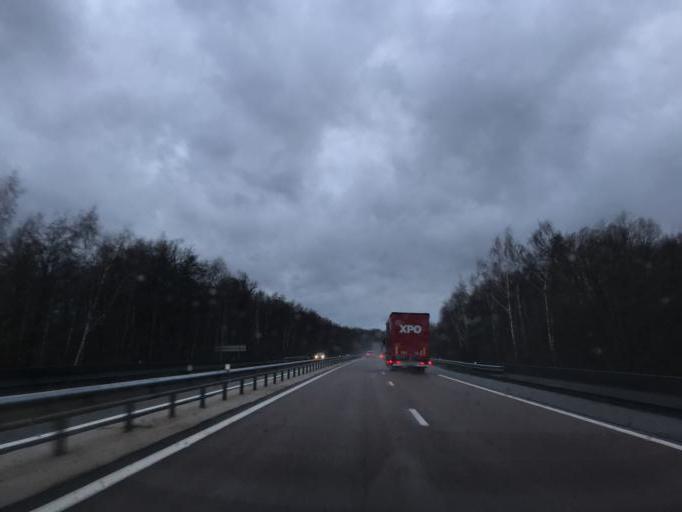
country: FR
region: Franche-Comte
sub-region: Departement du Jura
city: Damparis
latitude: 47.0911
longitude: 5.4112
